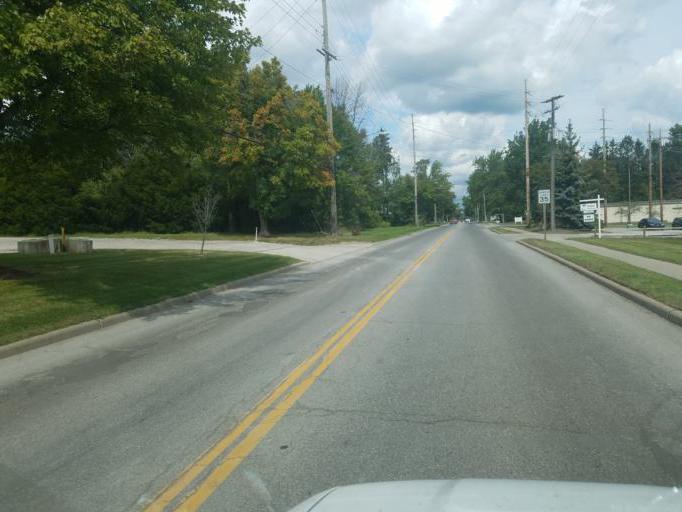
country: US
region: Ohio
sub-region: Geauga County
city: Middlefield
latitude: 41.4529
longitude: -81.0732
